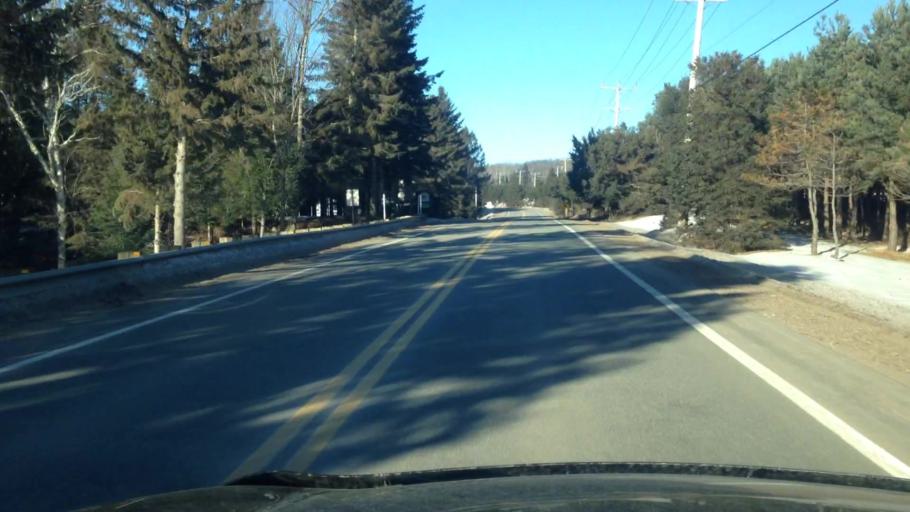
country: CA
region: Quebec
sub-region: Laurentides
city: Mont-Tremblant
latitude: 46.0458
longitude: -74.6084
